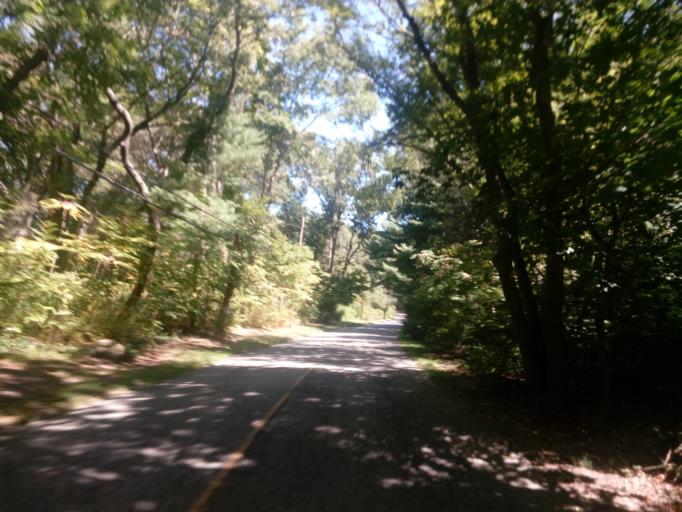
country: US
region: New York
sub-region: Nassau County
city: Upper Brookville
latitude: 40.8456
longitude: -73.5692
